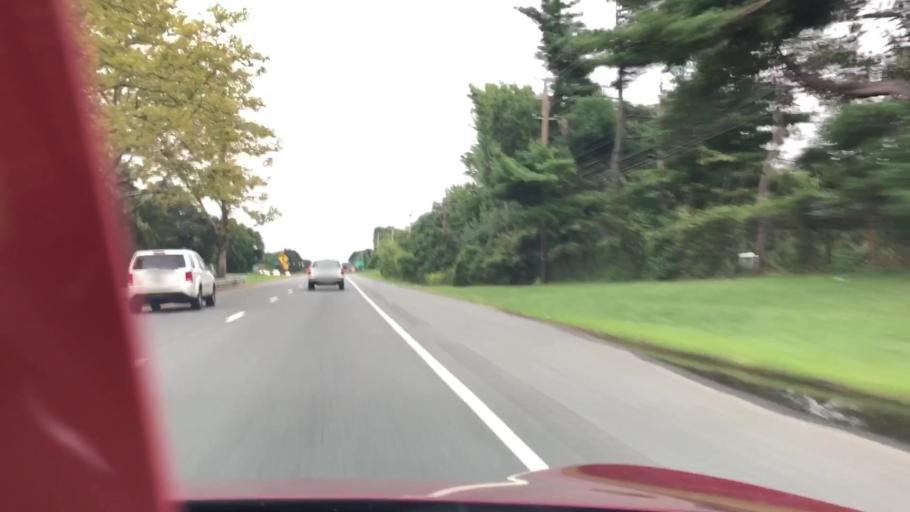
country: US
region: Delaware
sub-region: New Castle County
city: Glasgow
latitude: 39.6065
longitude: -75.7350
